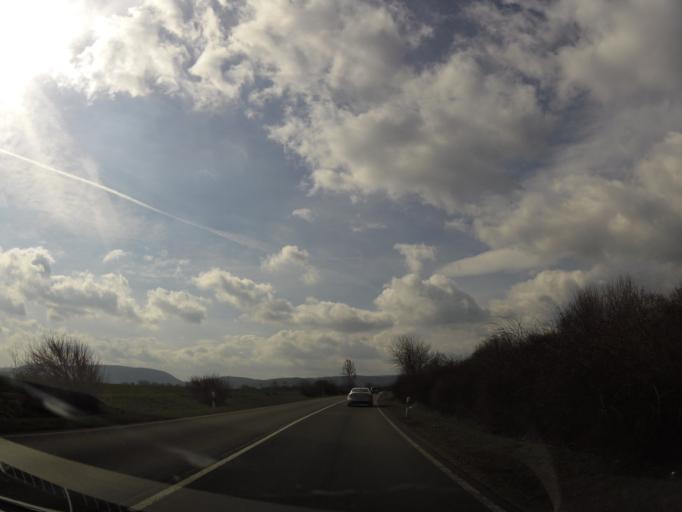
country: DE
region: Thuringia
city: Hohenkirchen
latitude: 50.8355
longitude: 10.7211
